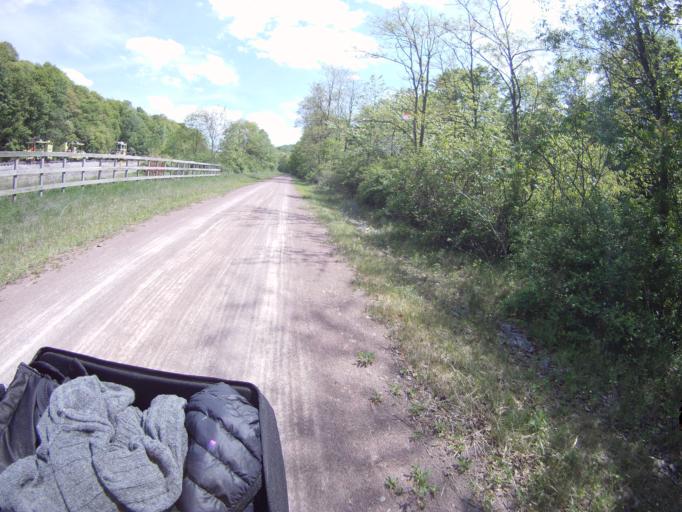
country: US
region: Pennsylvania
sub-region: Somerset County
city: Meyersdale
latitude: 39.8022
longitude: -78.9845
